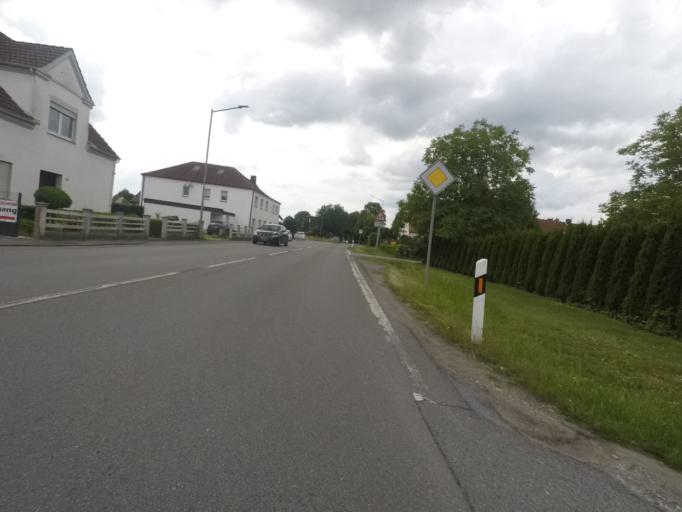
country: DE
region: North Rhine-Westphalia
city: Buende
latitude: 52.2053
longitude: 8.5444
